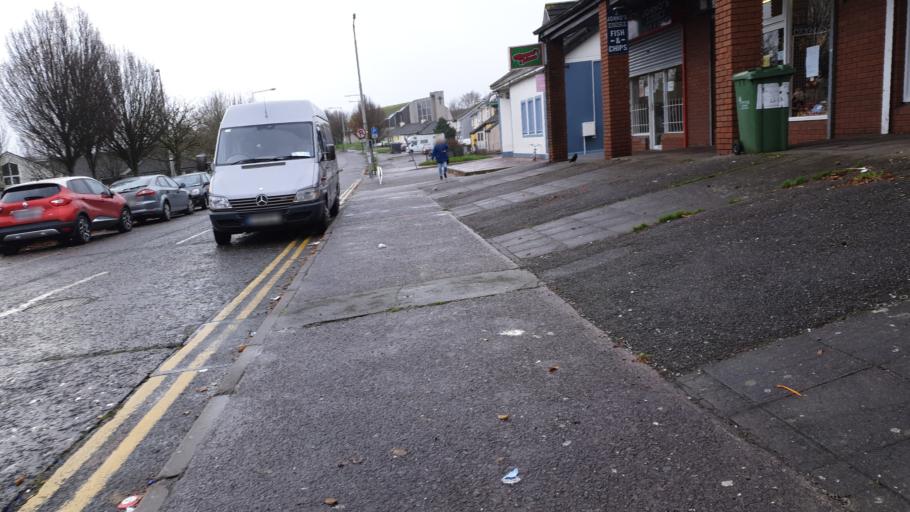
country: IE
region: Munster
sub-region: County Cork
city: Passage West
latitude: 51.8932
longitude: -8.4033
